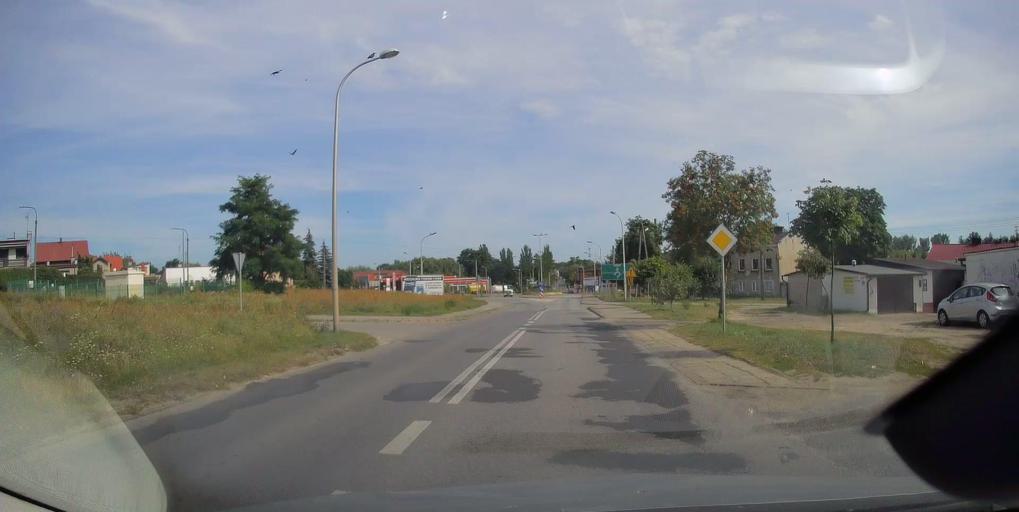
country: PL
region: Lodz Voivodeship
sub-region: Powiat tomaszowski
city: Tomaszow Mazowiecki
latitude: 51.5406
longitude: 19.9999
